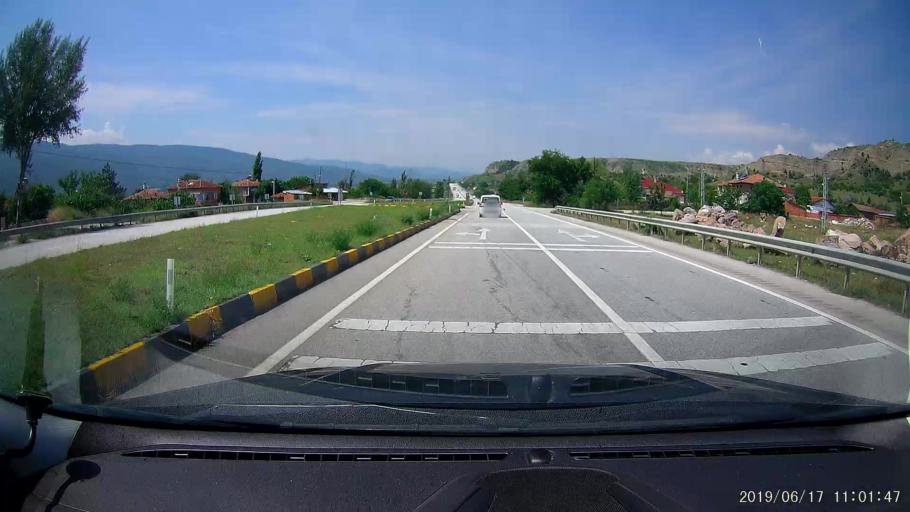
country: TR
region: Kastamonu
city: Tosya
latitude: 41.0242
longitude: 34.1482
